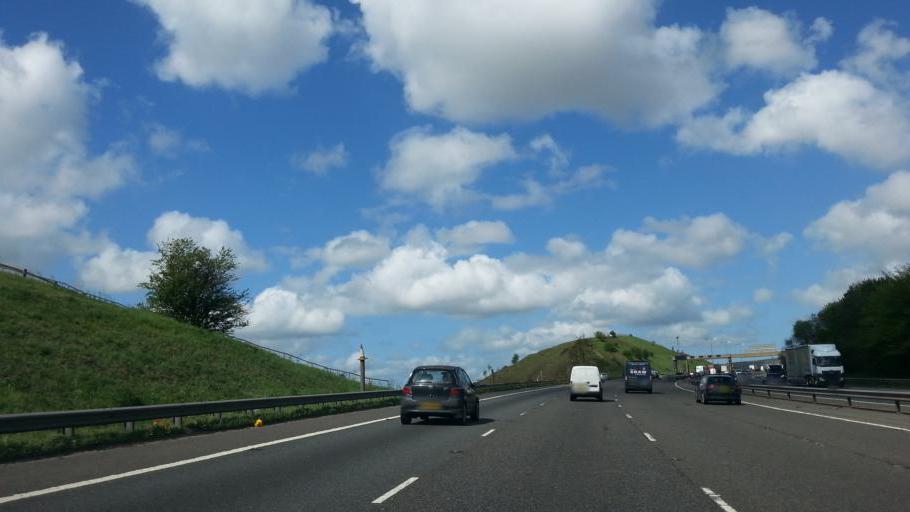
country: GB
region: England
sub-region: Borough of Rochdale
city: Milnrow
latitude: 53.6166
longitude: -2.0881
